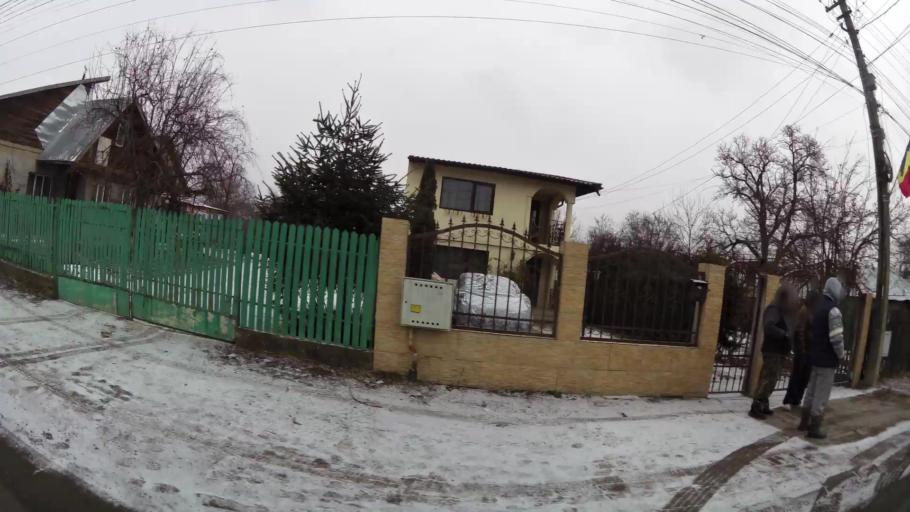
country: RO
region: Dambovita
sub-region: Municipiul Targoviste
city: Targoviste
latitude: 44.9413
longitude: 25.4620
